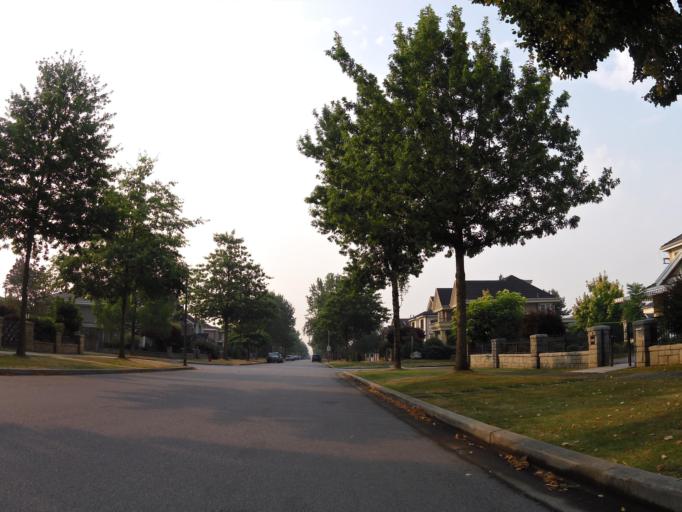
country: CA
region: British Columbia
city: Vancouver
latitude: 49.2222
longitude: -123.1482
